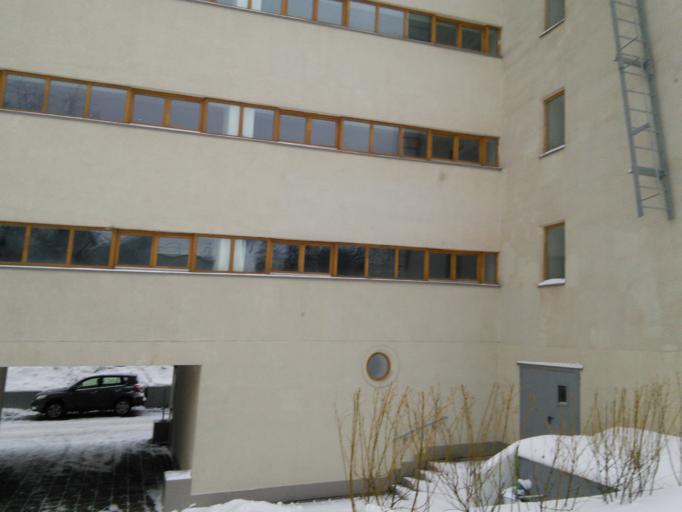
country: RU
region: Moscow
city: Novyye Cheremushki
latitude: 55.7116
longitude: 37.5955
